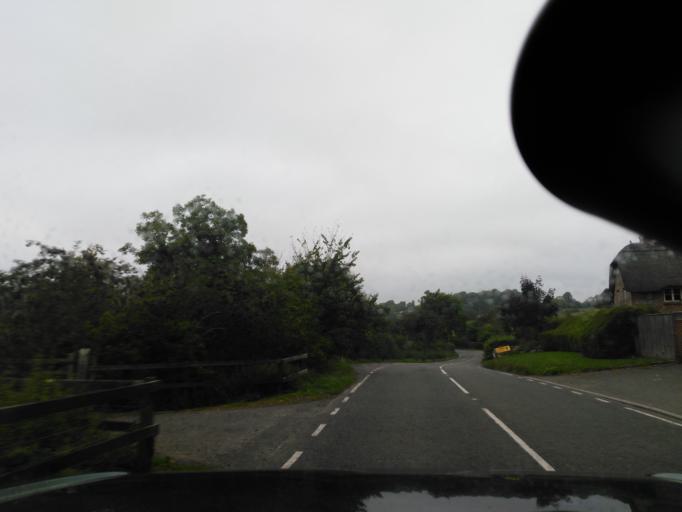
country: GB
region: England
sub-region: Dorset
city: Blandford Forum
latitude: 50.8923
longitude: -2.1941
